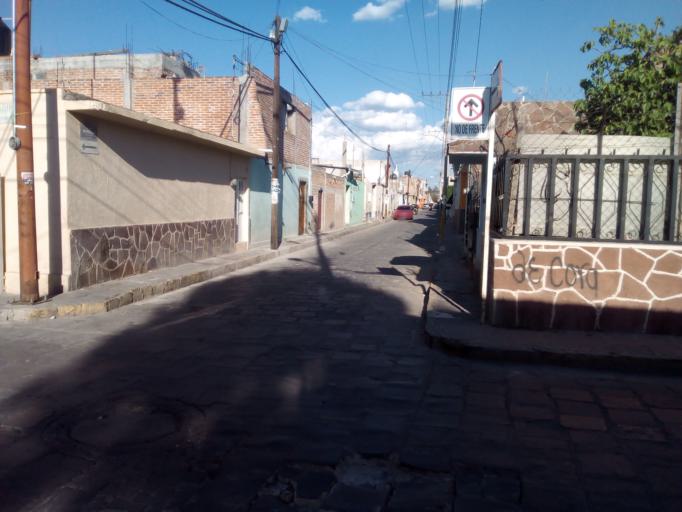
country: MX
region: Guerrero
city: San Luis de la Paz
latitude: 21.2994
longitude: -100.5222
